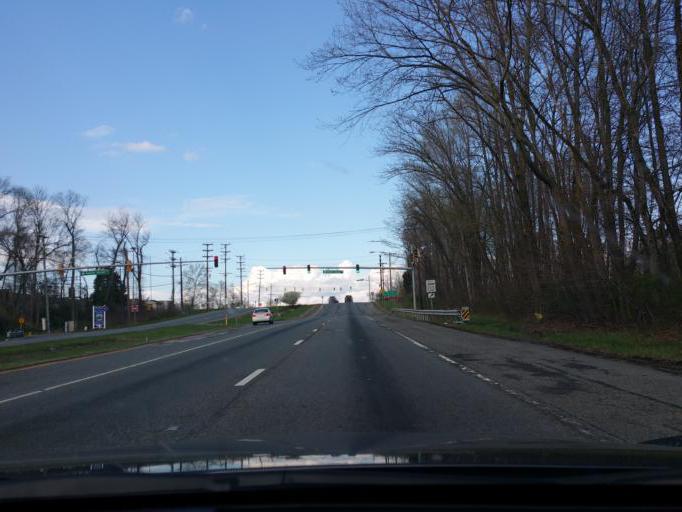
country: US
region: Maryland
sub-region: Harford County
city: Aberdeen
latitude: 39.5234
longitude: -76.1407
